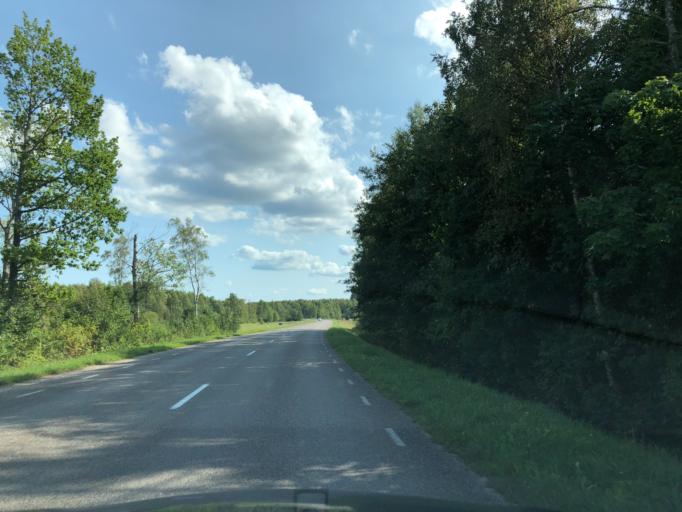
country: EE
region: Hiiumaa
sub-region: Kaerdla linn
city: Kardla
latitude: 58.7235
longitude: 22.5619
